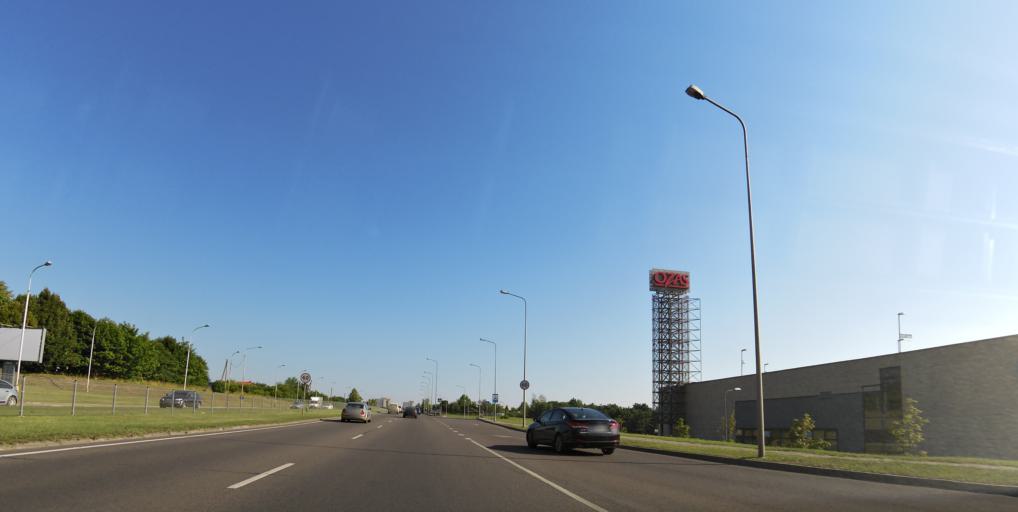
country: LT
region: Vilnius County
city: Seskine
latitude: 54.7138
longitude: 25.2708
